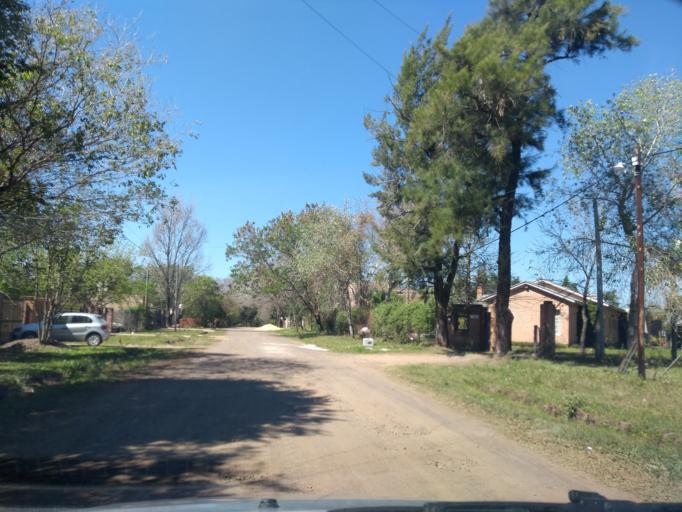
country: AR
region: Chaco
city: Resistencia
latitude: -27.4320
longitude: -58.9487
